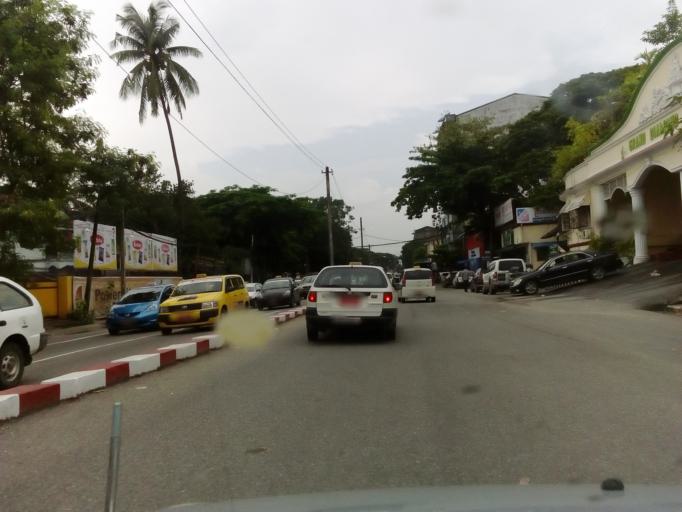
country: MM
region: Yangon
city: Yangon
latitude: 16.8030
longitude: 96.1748
